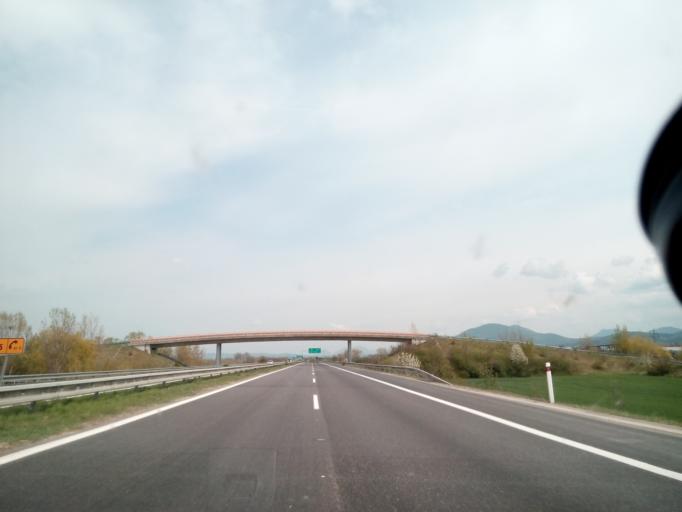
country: SK
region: Nitriansky
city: Ilava
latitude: 48.9902
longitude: 18.2040
